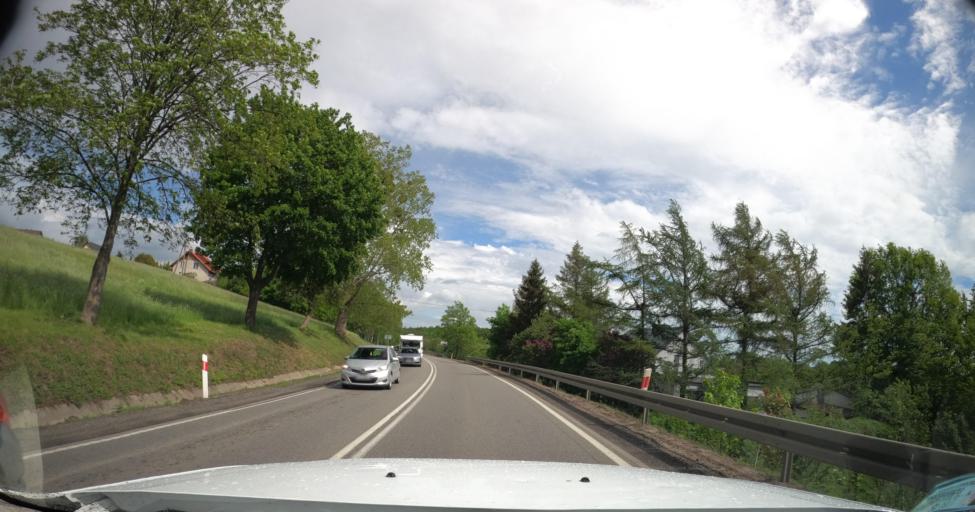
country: PL
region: Pomeranian Voivodeship
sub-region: Powiat kartuski
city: Zukowo
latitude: 54.3397
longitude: 18.3783
